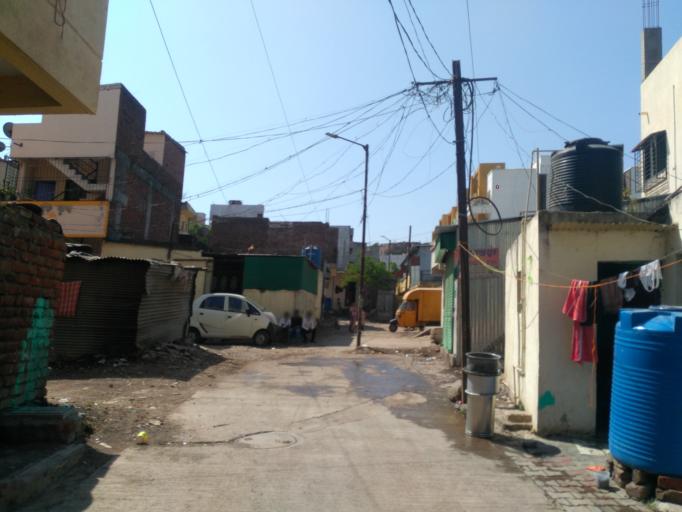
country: IN
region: Maharashtra
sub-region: Pune Division
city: Pune
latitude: 18.4465
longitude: 73.8772
